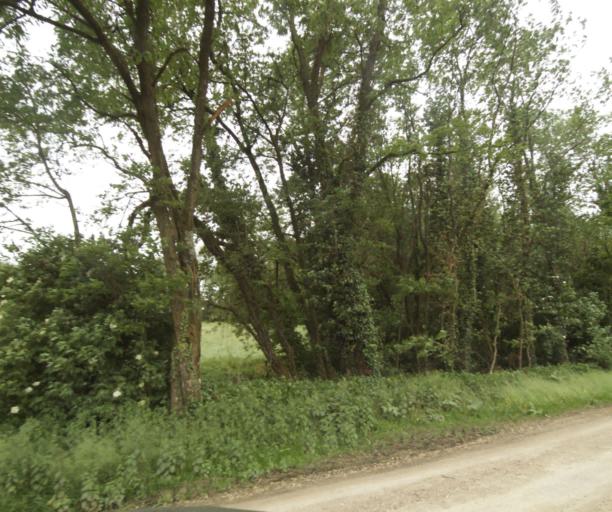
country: FR
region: Rhone-Alpes
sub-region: Departement du Rhone
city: Rillieux-la-Pape
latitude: 45.8468
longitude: 4.9214
